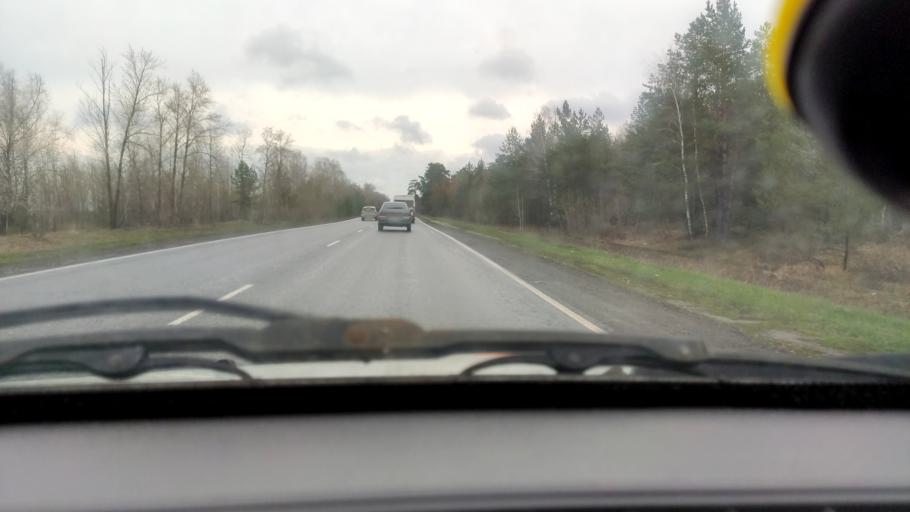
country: RU
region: Samara
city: Povolzhskiy
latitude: 53.6181
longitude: 49.6347
